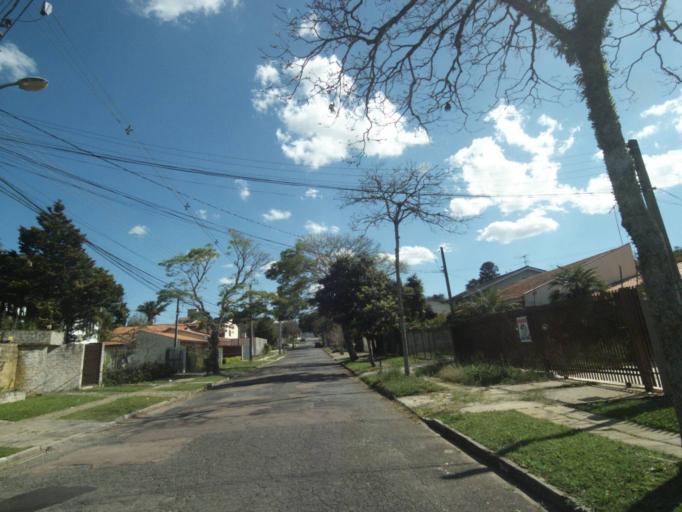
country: BR
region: Parana
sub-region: Curitiba
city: Curitiba
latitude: -25.3852
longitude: -49.2421
